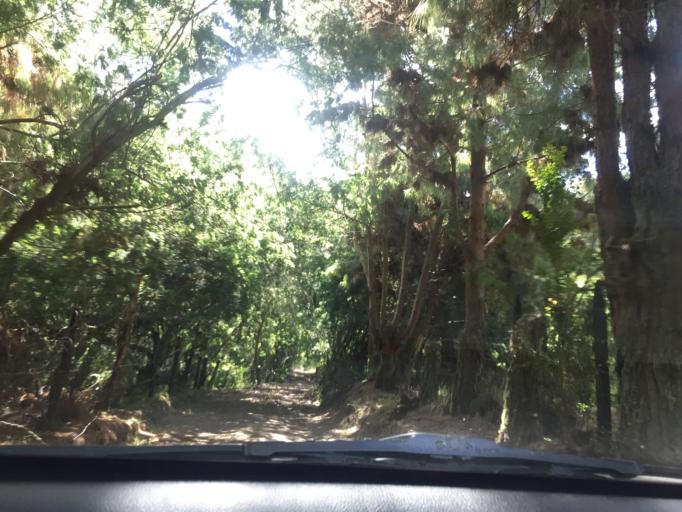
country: CO
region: Cundinamarca
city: Tocancipa
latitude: 4.9542
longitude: -73.8830
